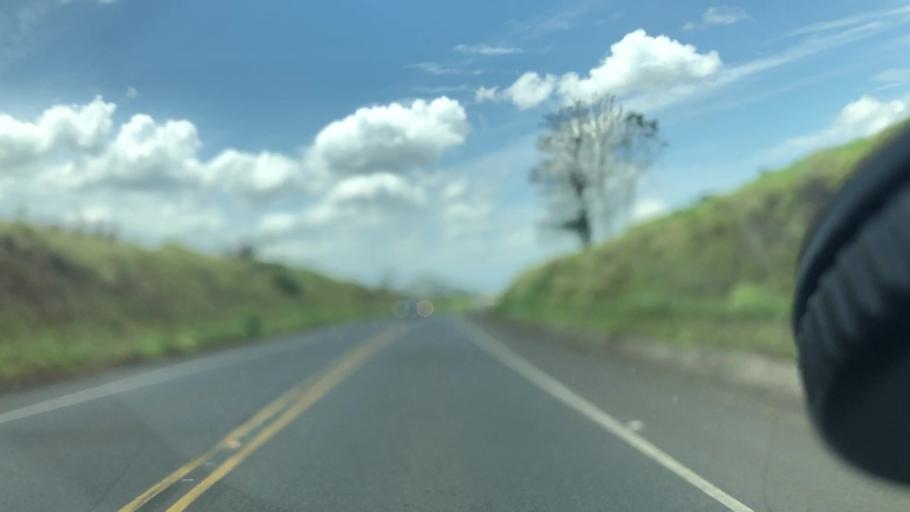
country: CR
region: Alajuela
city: Pital
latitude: 10.4344
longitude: -84.2814
